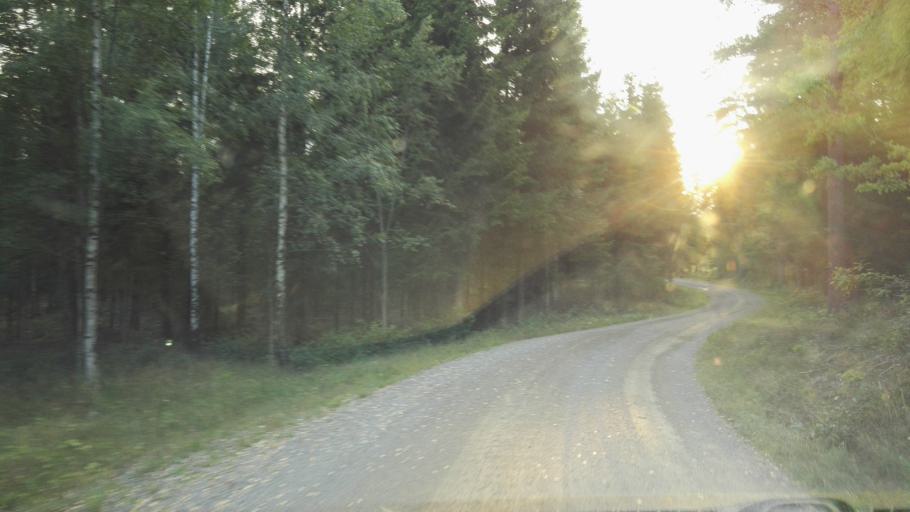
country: SE
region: Joenkoeping
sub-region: Vetlanda Kommun
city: Landsbro
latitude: 57.2557
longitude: 14.8971
